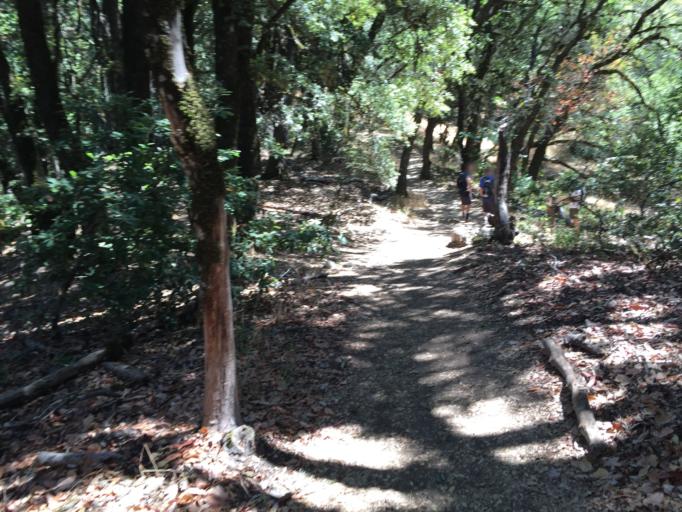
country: US
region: California
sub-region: Santa Clara County
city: Saratoga
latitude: 37.2303
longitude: -122.1135
